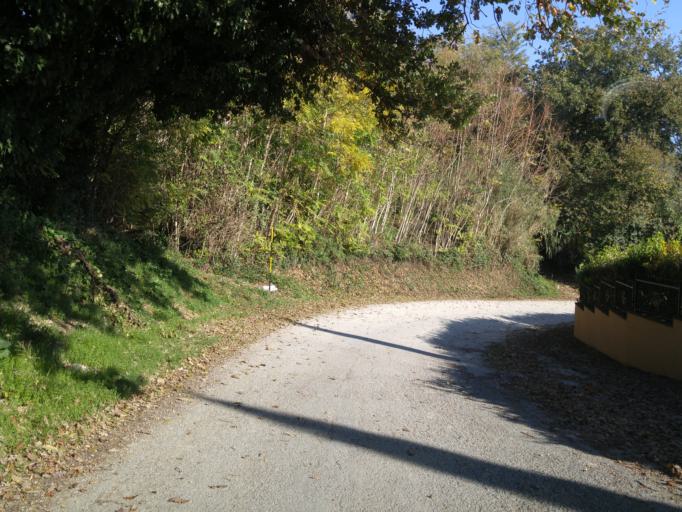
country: IT
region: The Marches
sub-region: Provincia di Pesaro e Urbino
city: Montemaggiore al Metauro
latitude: 43.7339
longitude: 12.9399
